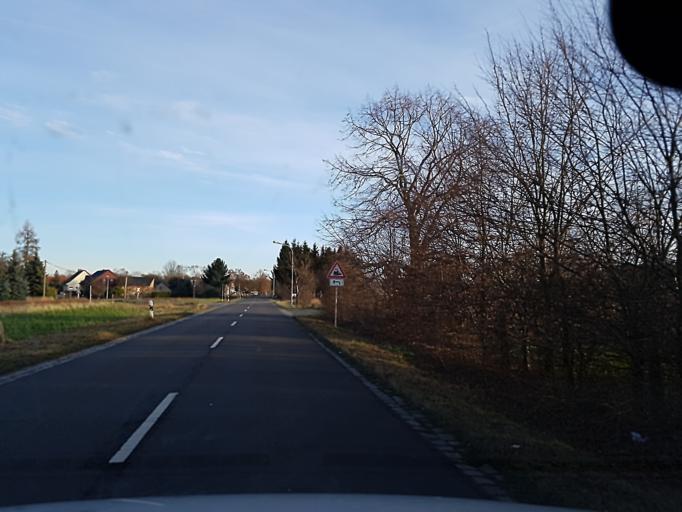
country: DE
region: Brandenburg
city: Finsterwalde
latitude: 51.6148
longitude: 13.7557
